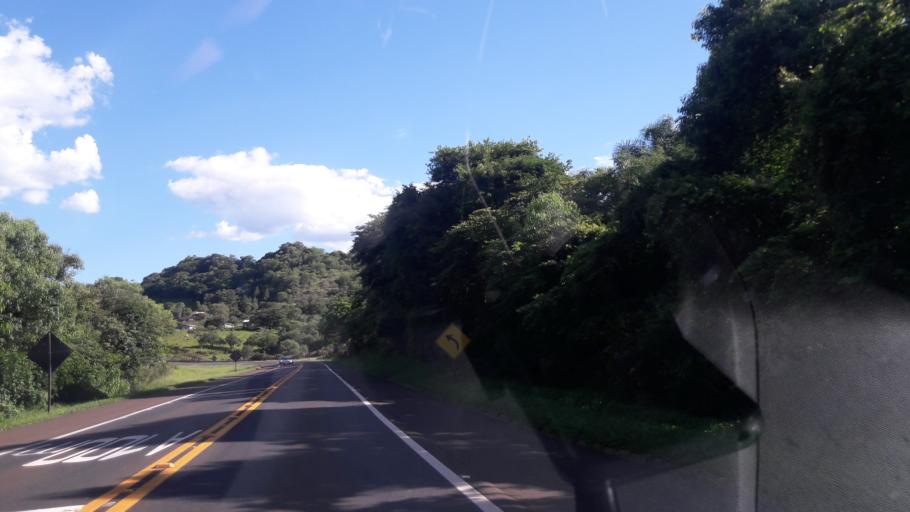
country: BR
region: Parana
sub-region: Laranjeiras Do Sul
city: Laranjeiras do Sul
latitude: -25.4196
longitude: -52.0310
